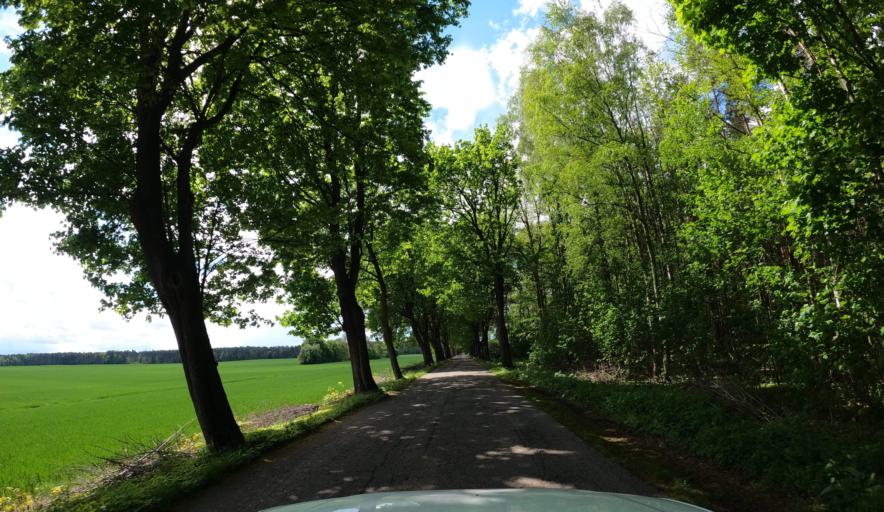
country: PL
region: West Pomeranian Voivodeship
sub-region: Powiat kamienski
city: Wolin
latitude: 53.8864
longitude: 14.6580
